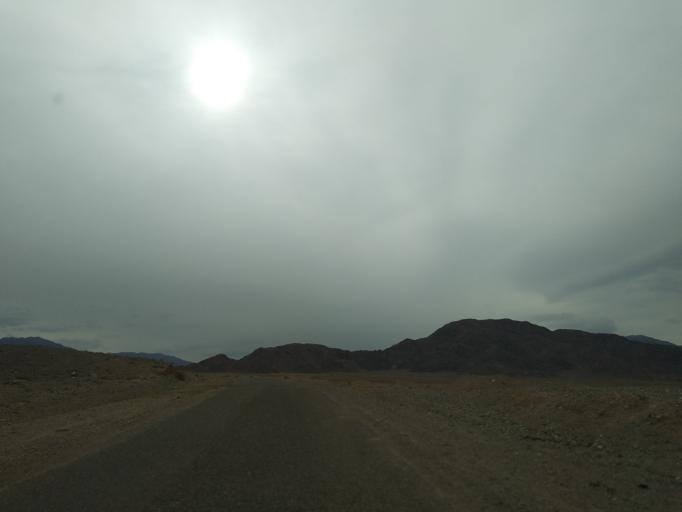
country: KG
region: Ysyk-Koel
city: Balykchy
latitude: 42.3201
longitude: 76.1740
